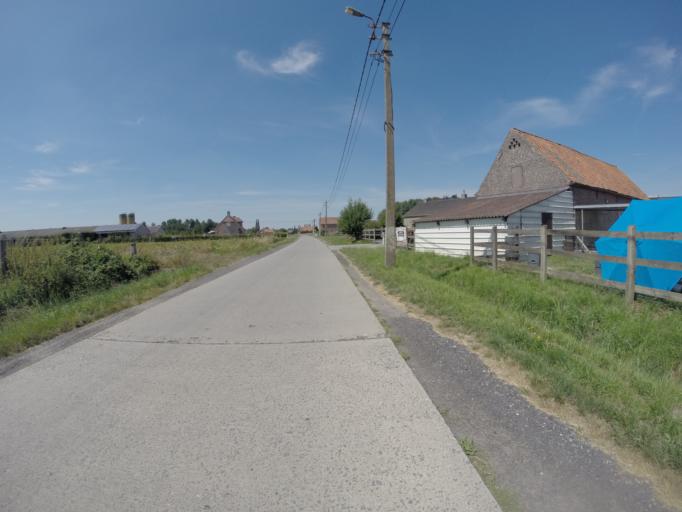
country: BE
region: Flanders
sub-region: Provincie Oost-Vlaanderen
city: Knesselare
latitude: 51.1287
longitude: 3.4015
